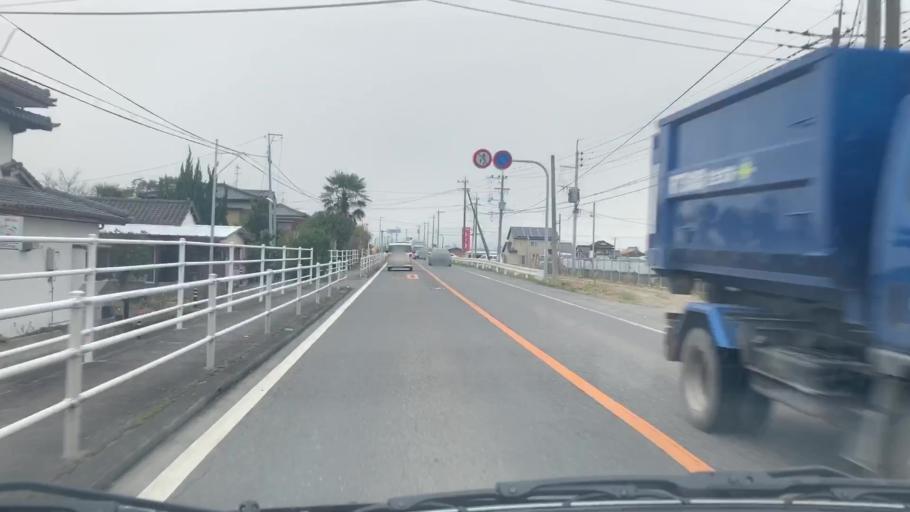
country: JP
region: Saga Prefecture
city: Saga-shi
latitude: 33.1919
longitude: 130.1929
